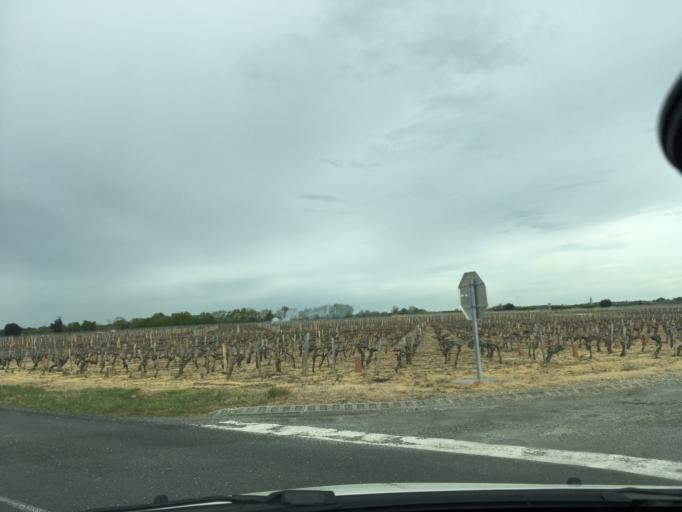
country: FR
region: Aquitaine
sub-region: Departement de la Gironde
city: Lesparre-Medoc
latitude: 45.3260
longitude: -0.8837
